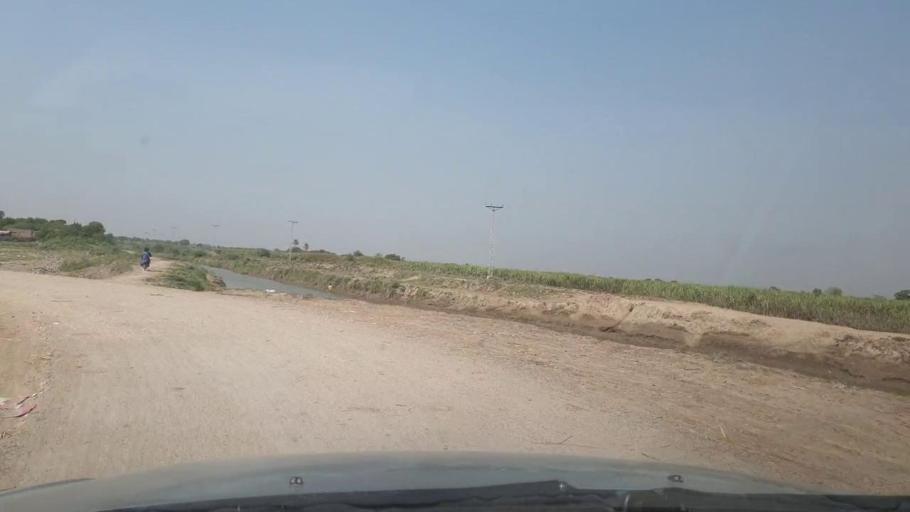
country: PK
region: Sindh
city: Bulri
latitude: 24.8662
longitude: 68.3331
